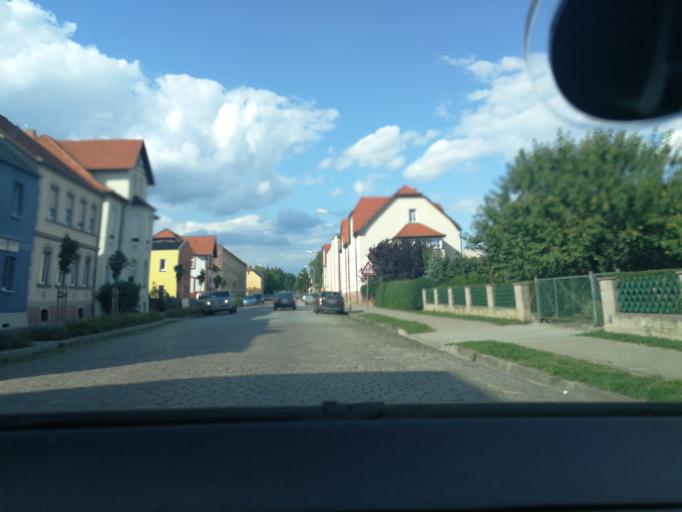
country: DE
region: Brandenburg
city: Pritzwalk
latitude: 53.1540
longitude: 12.1790
